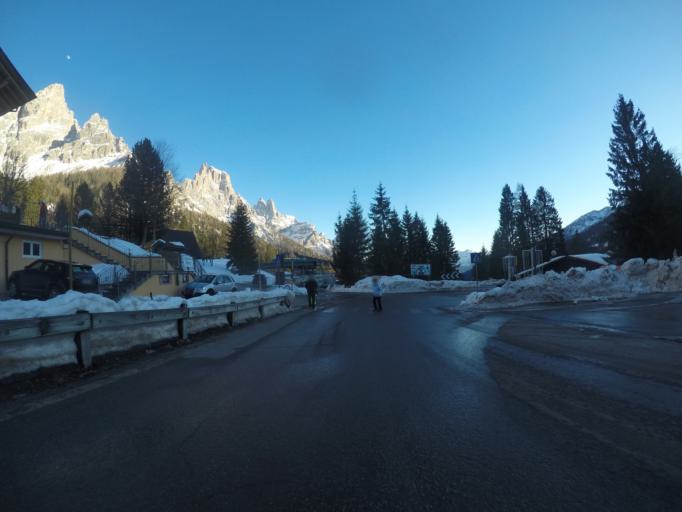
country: IT
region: Trentino-Alto Adige
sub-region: Provincia di Trento
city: Siror
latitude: 46.2648
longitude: 11.8045
